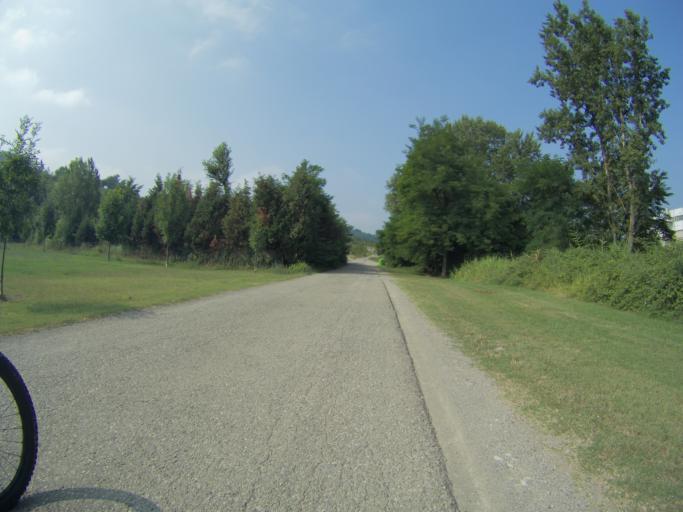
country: IT
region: Emilia-Romagna
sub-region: Provincia di Reggio Emilia
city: Ventoso
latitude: 44.5856
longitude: 10.6708
